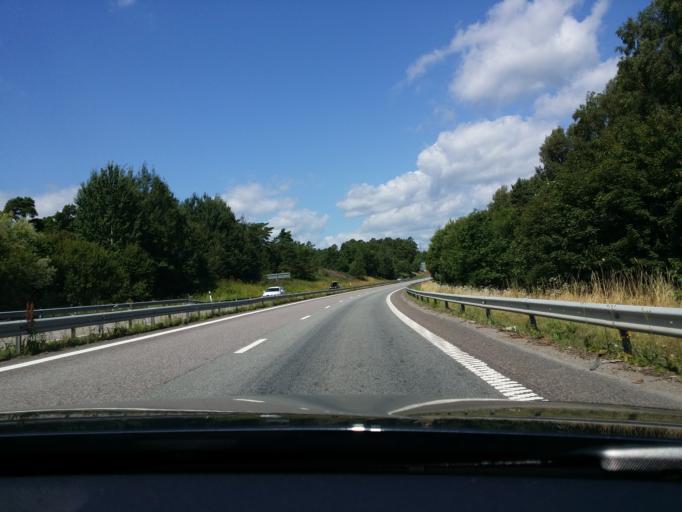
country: SE
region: Blekinge
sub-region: Solvesborgs Kommun
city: Soelvesborg
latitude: 56.0655
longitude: 14.5506
